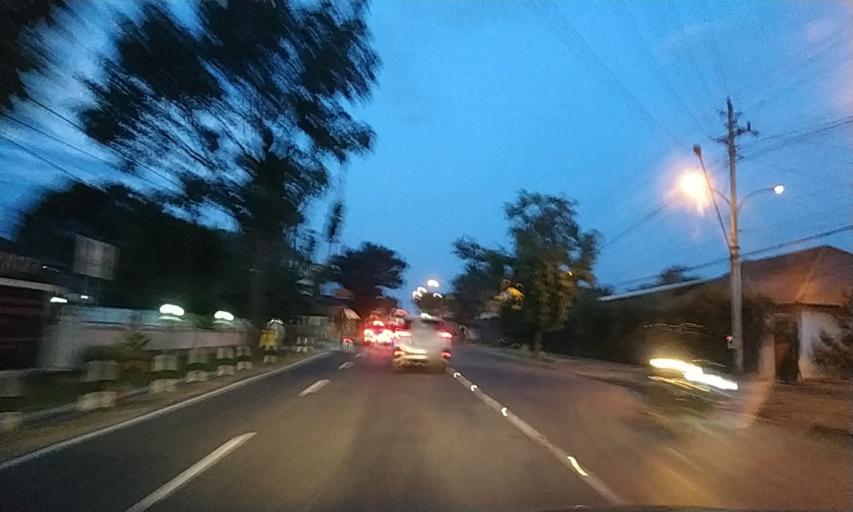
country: ID
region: Daerah Istimewa Yogyakarta
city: Godean
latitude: -7.8135
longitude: 110.2614
